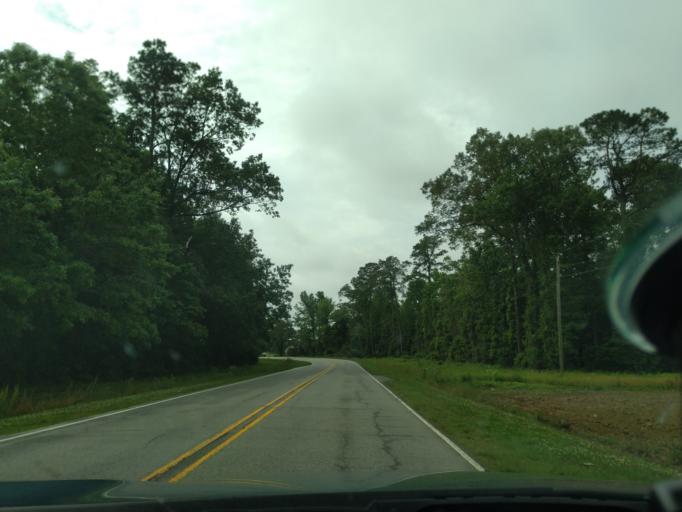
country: US
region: North Carolina
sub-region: Washington County
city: Plymouth
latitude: 35.8974
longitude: -76.6096
